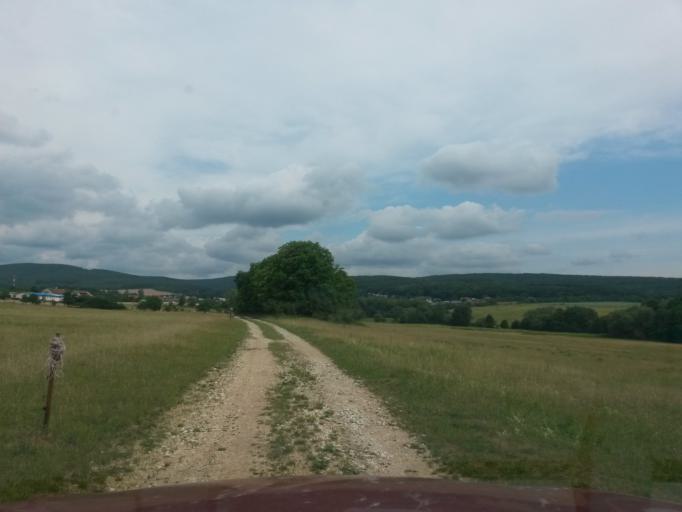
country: SK
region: Kosicky
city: Moldava nad Bodvou
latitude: 48.6655
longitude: 21.1122
